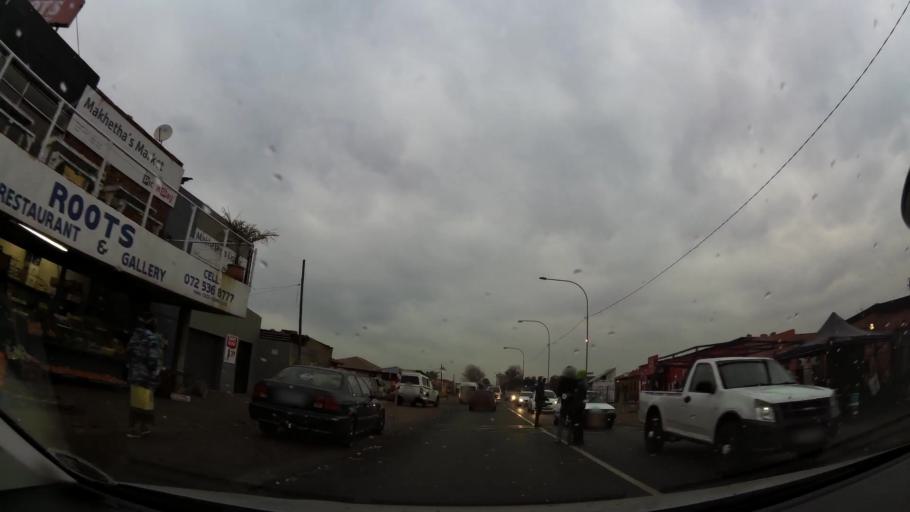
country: ZA
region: Gauteng
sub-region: City of Johannesburg Metropolitan Municipality
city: Soweto
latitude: -26.2454
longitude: 27.8707
